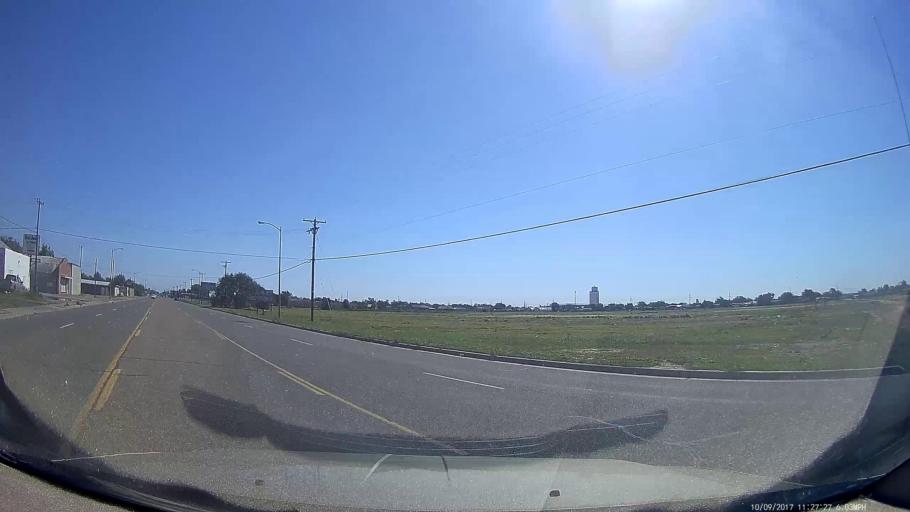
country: US
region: New Mexico
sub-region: Curry County
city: Clovis
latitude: 34.4047
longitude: -103.2267
